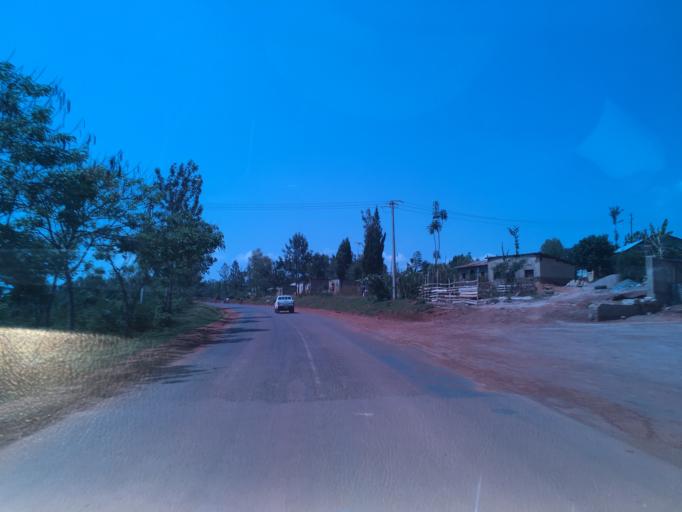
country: RW
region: Eastern Province
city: Rwamagana
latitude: -1.9174
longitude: 30.4931
